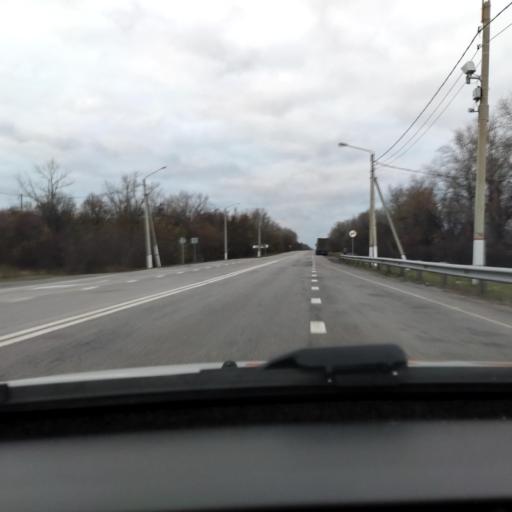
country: RU
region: Lipetsk
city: Khlevnoye
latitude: 52.2683
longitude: 39.1687
